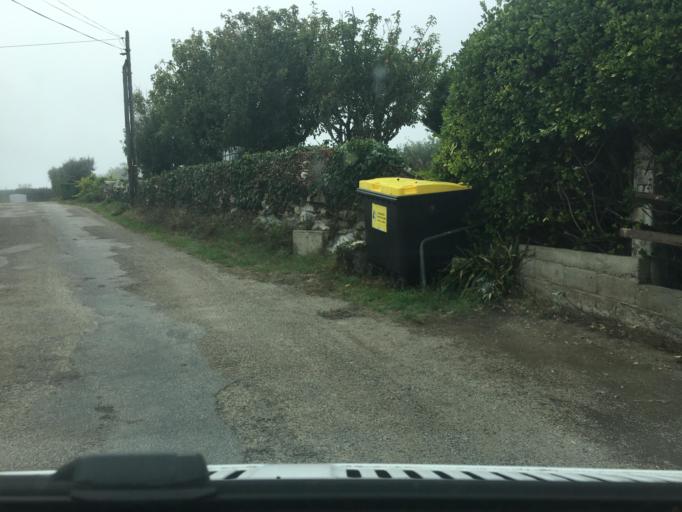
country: FR
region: Brittany
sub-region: Departement du Finistere
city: Plogoff
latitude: 48.0329
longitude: -4.6973
